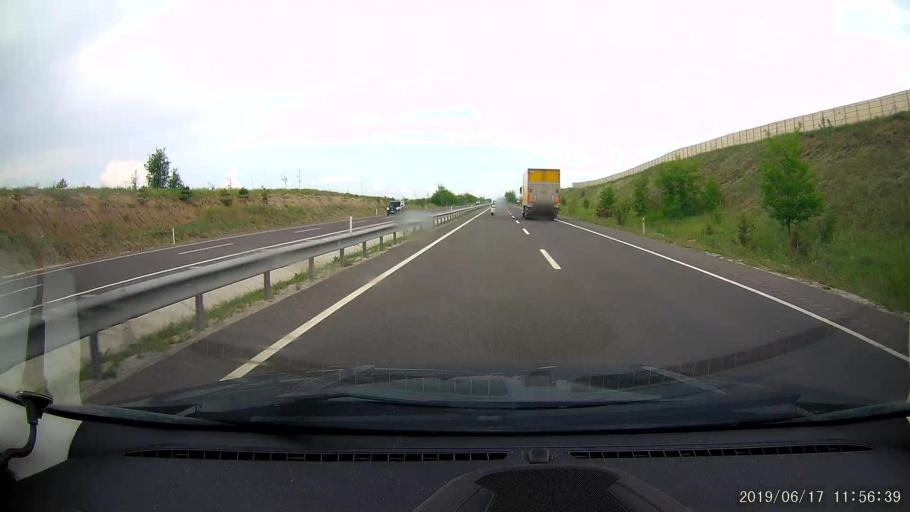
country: TR
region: Cankiri
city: Cerkes
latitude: 40.8042
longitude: 32.9773
